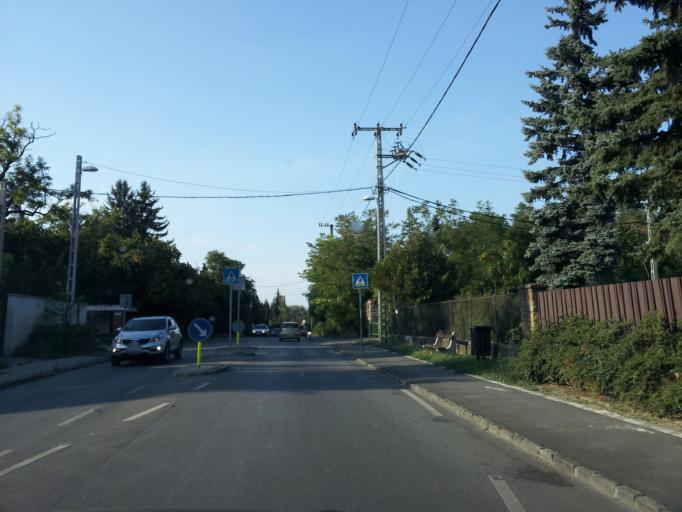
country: HU
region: Pest
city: Leanyfalu
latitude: 47.6976
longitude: 19.0885
